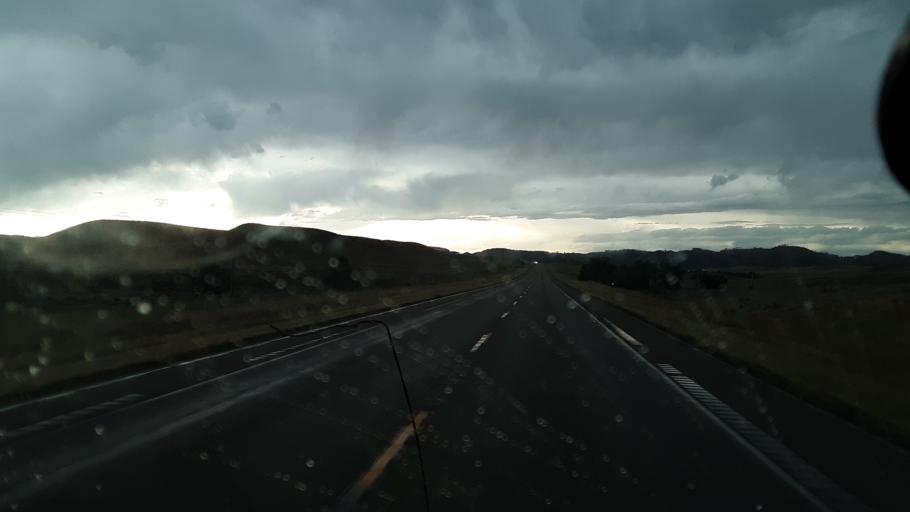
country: US
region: Montana
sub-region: Powder River County
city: Broadus
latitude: 45.5417
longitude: -105.8286
